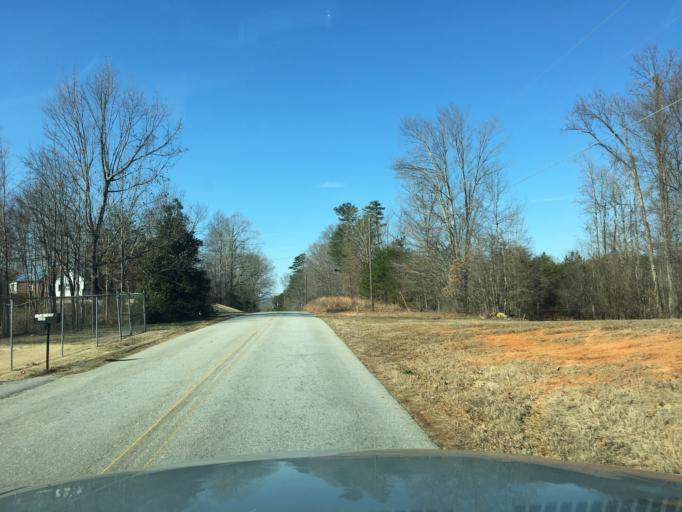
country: US
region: South Carolina
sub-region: Pickens County
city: Arial
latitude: 34.8738
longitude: -82.6543
